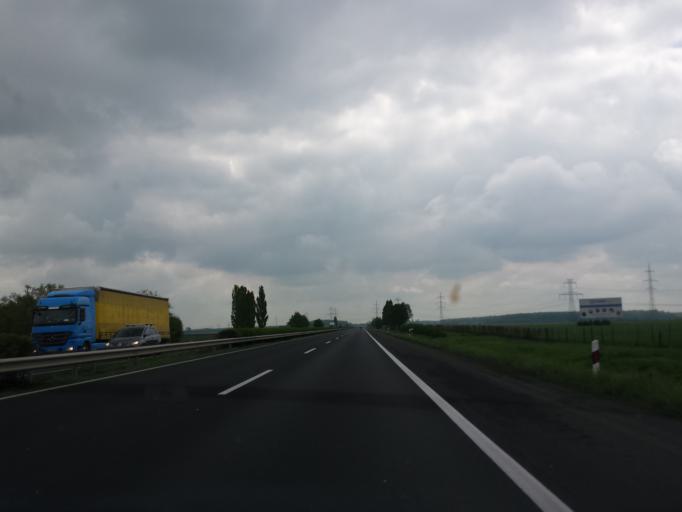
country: HU
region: Gyor-Moson-Sopron
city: Mosonmagyarovar
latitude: 47.8280
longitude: 17.2788
